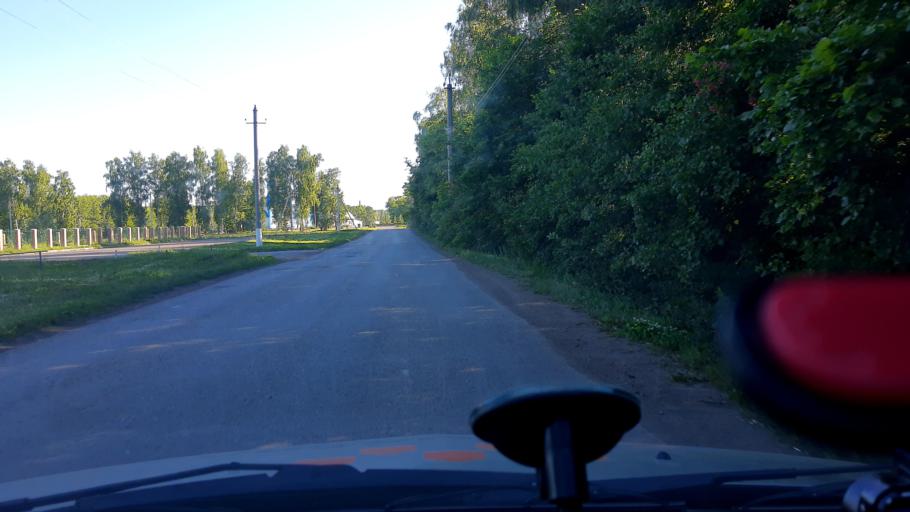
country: RU
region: Bashkortostan
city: Chishmy
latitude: 54.5940
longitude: 55.3667
